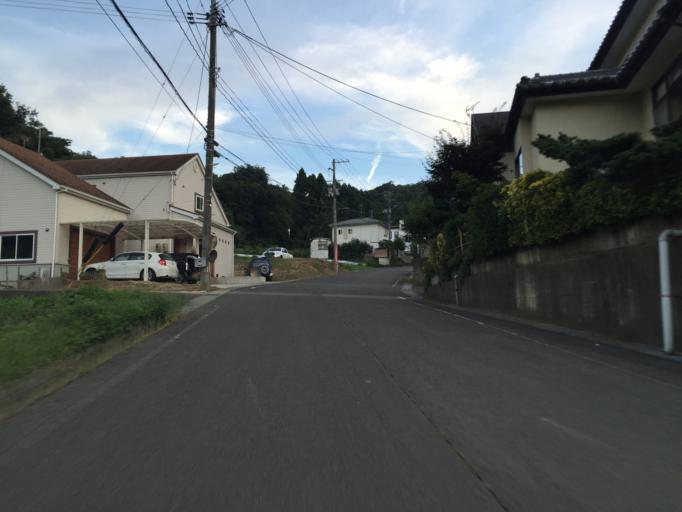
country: JP
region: Fukushima
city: Fukushima-shi
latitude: 37.7374
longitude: 140.4884
